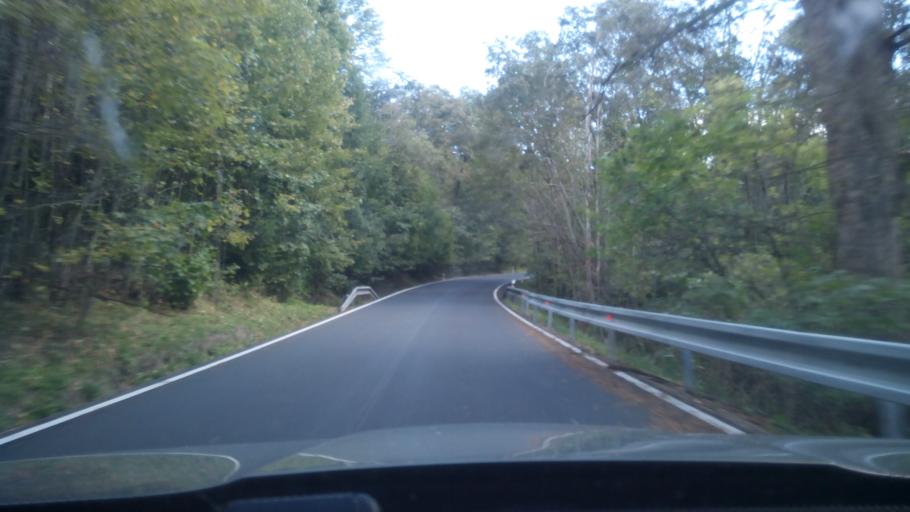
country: CZ
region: Plzensky
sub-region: Okres Klatovy
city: Kasperske Hory
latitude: 49.1409
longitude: 13.6031
